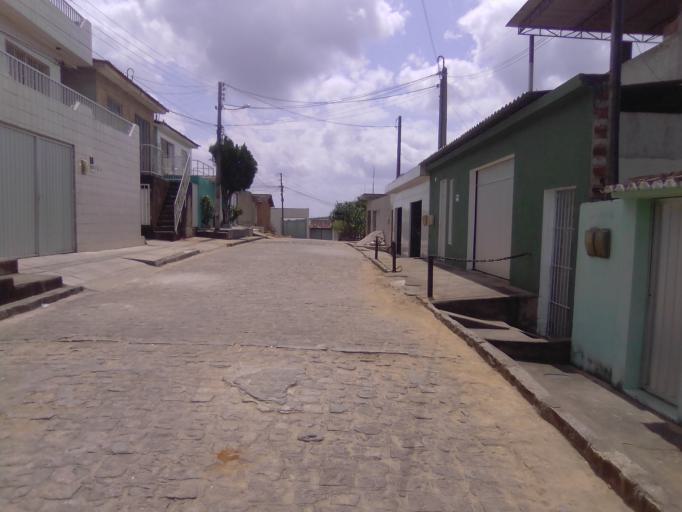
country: BR
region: Pernambuco
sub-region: Vicencia
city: Vicencia
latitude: -7.6624
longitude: -35.3231
